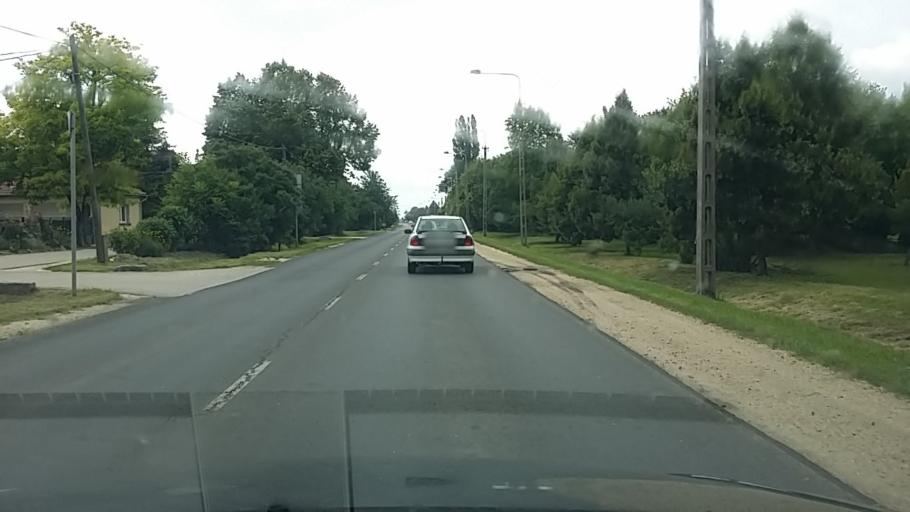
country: HU
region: Pest
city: Orkeny
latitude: 47.1289
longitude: 19.4249
